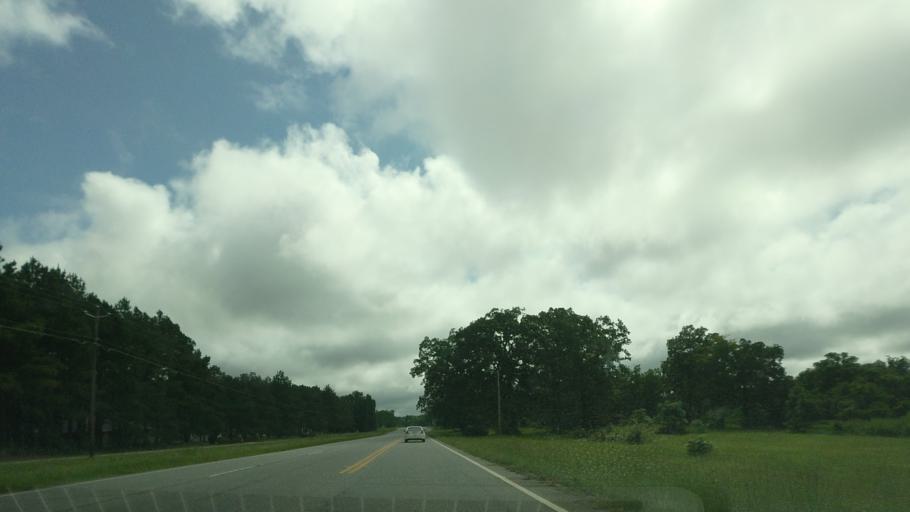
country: US
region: Georgia
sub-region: Laurens County
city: Dublin
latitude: 32.5507
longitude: -82.9967
